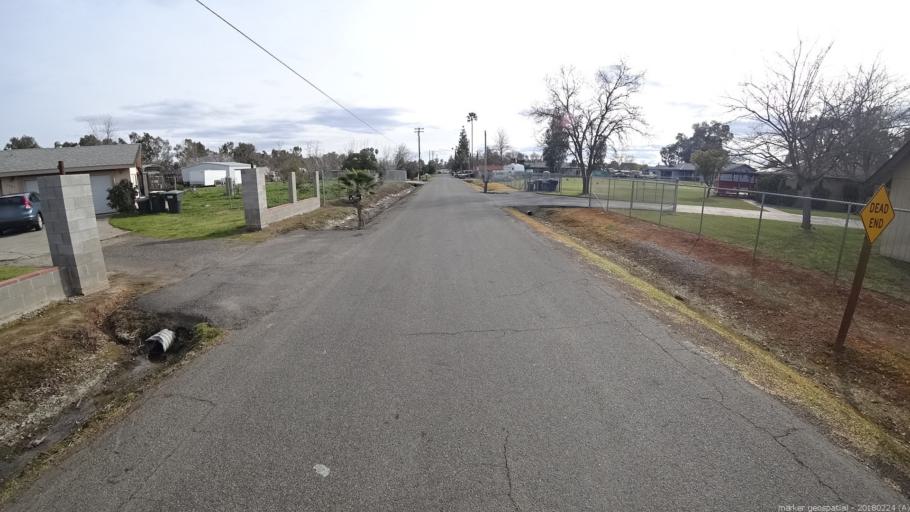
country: US
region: California
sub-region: Sacramento County
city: Elverta
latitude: 38.7099
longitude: -121.4573
